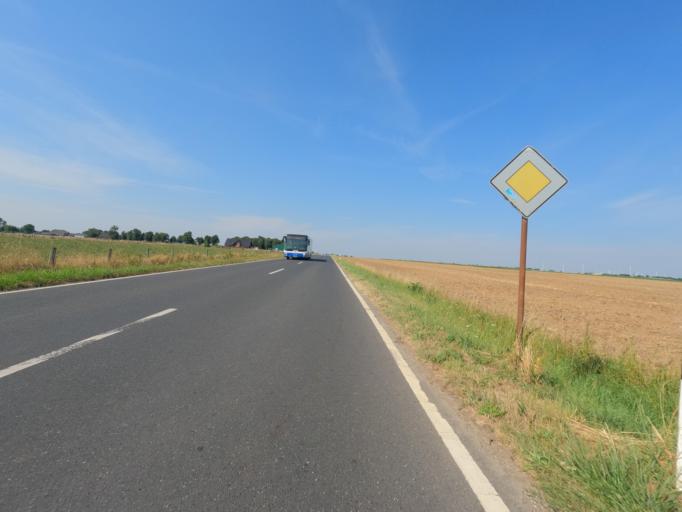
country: DE
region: North Rhine-Westphalia
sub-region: Regierungsbezirk Koln
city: Titz
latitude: 50.9872
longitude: 6.3691
